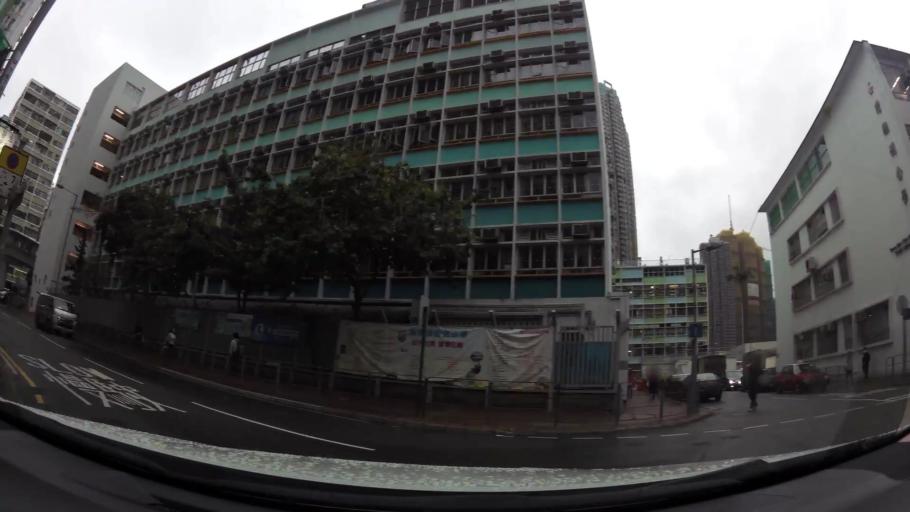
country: HK
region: Tsuen Wan
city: Tsuen Wan
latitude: 22.3724
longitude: 114.1150
